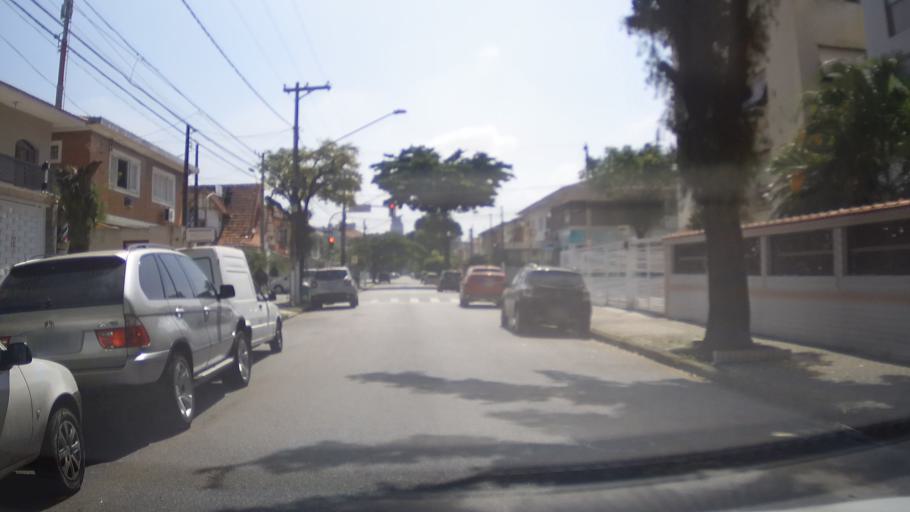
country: BR
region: Sao Paulo
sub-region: Santos
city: Santos
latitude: -23.9795
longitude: -46.3080
